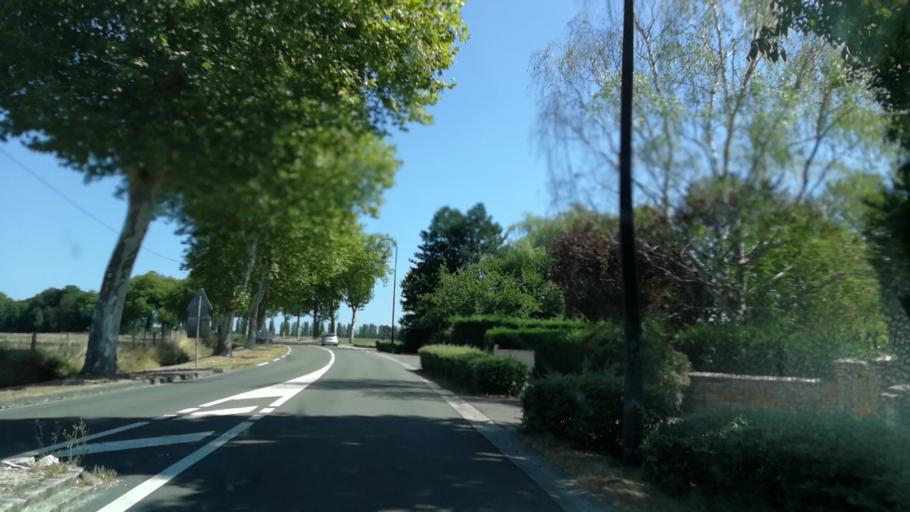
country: FR
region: Ile-de-France
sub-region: Departement des Yvelines
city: Cernay-la-Ville
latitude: 48.6748
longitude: 1.9811
